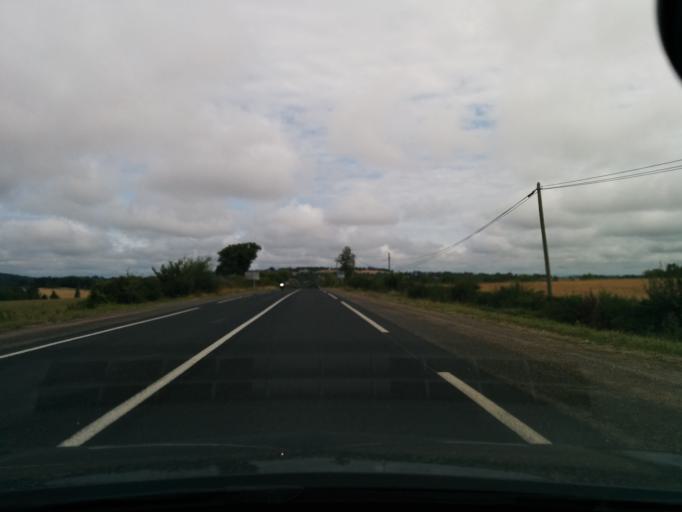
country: FR
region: Midi-Pyrenees
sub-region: Departement du Lot
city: Le Vigan
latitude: 44.7333
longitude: 1.5000
